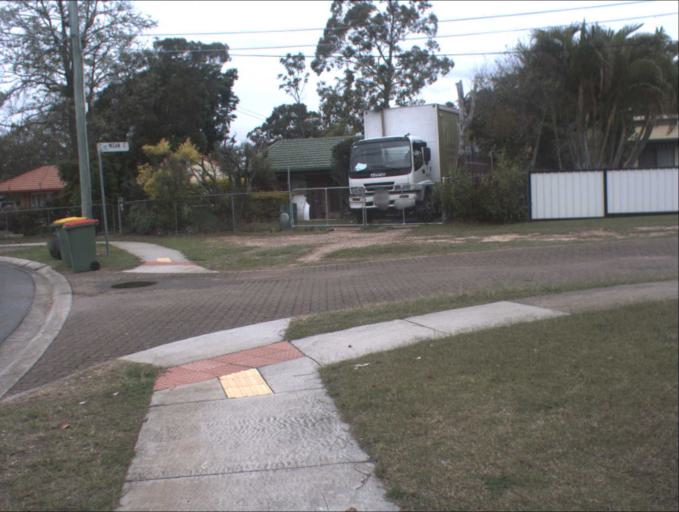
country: AU
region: Queensland
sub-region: Logan
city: Park Ridge South
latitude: -27.6822
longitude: 153.0196
